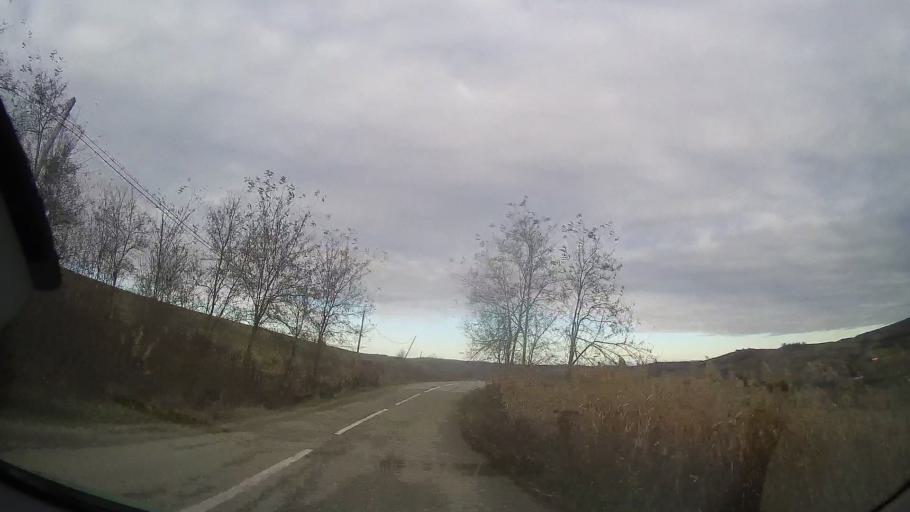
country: RO
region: Bistrita-Nasaud
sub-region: Comuna Micestii de Campie
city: Micestii de Campie
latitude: 46.8520
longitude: 24.3100
